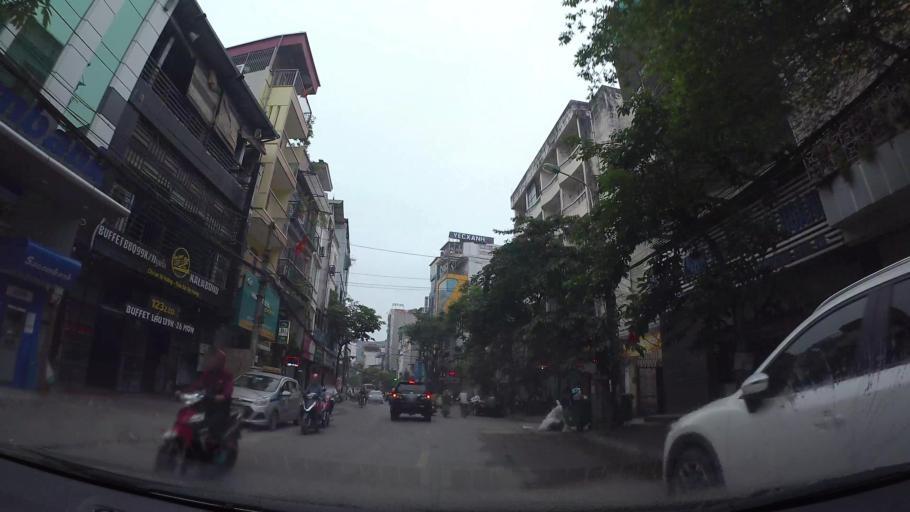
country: VN
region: Ha Noi
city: Hai BaTrung
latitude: 20.9954
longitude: 105.8428
